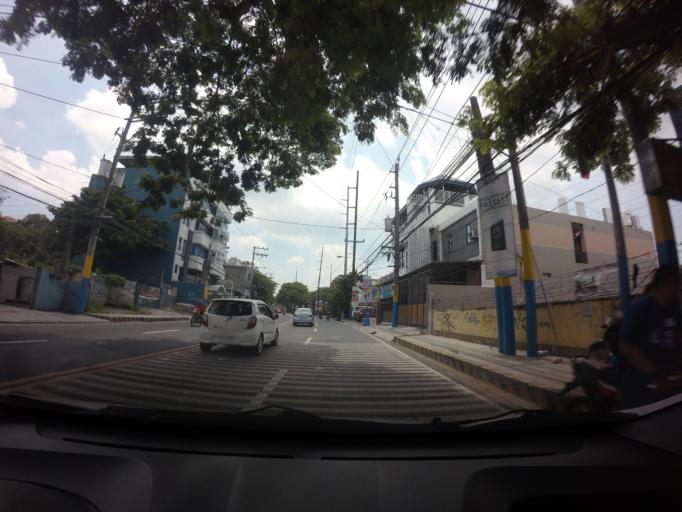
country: PH
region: Calabarzon
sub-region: Province of Laguna
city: San Pedro
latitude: 14.4010
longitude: 121.0470
